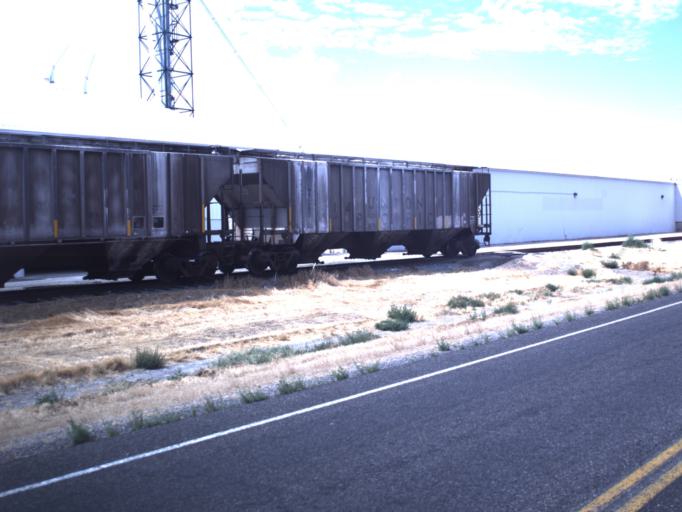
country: US
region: Utah
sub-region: Box Elder County
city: Honeyville
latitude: 41.5531
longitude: -112.1199
